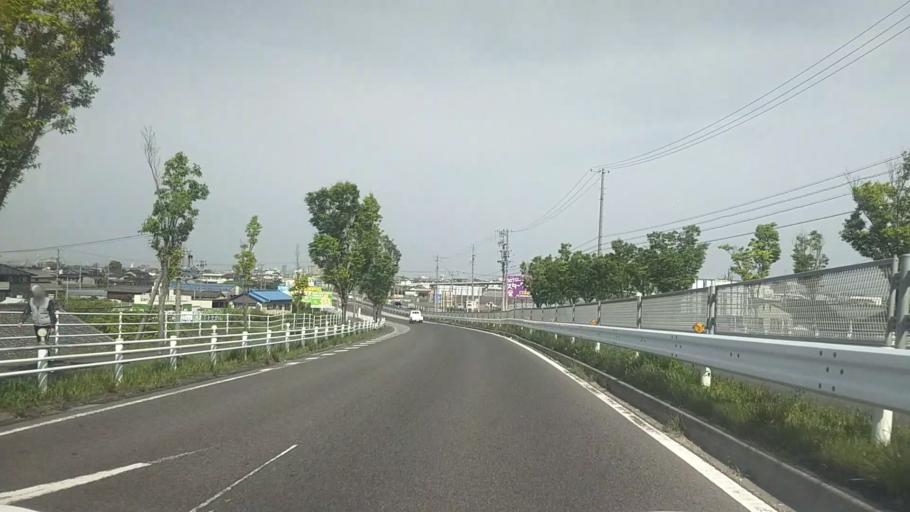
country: JP
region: Aichi
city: Okazaki
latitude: 34.9392
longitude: 137.1389
